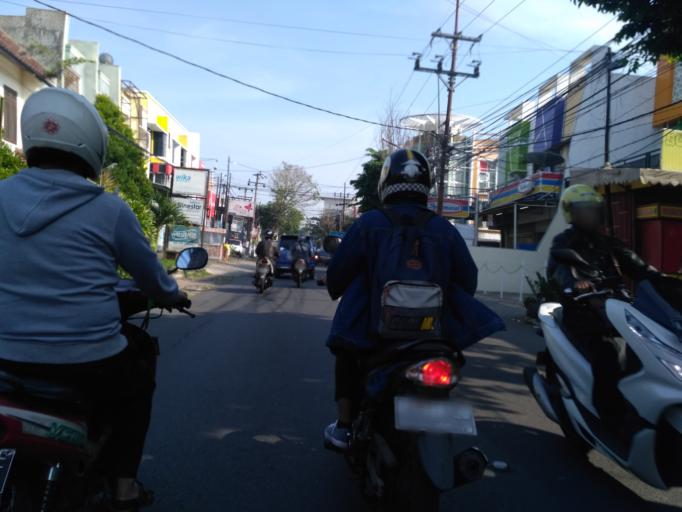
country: ID
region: East Java
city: Malang
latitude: -7.9452
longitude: 112.6205
